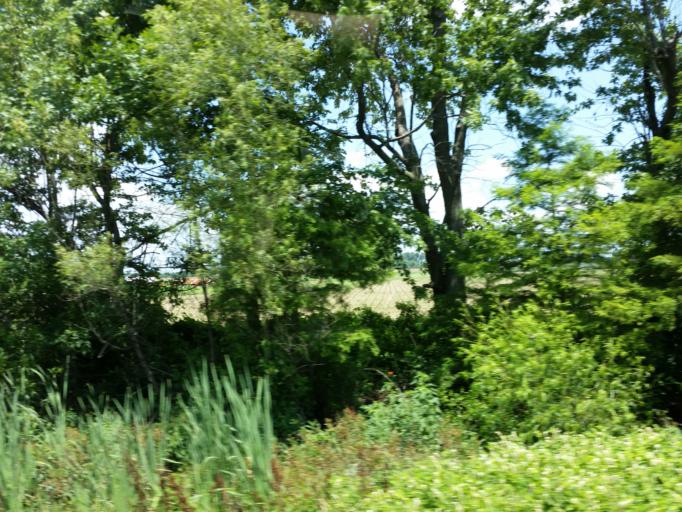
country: US
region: Kentucky
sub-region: Fulton County
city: Hickman
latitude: 36.5470
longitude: -89.2585
